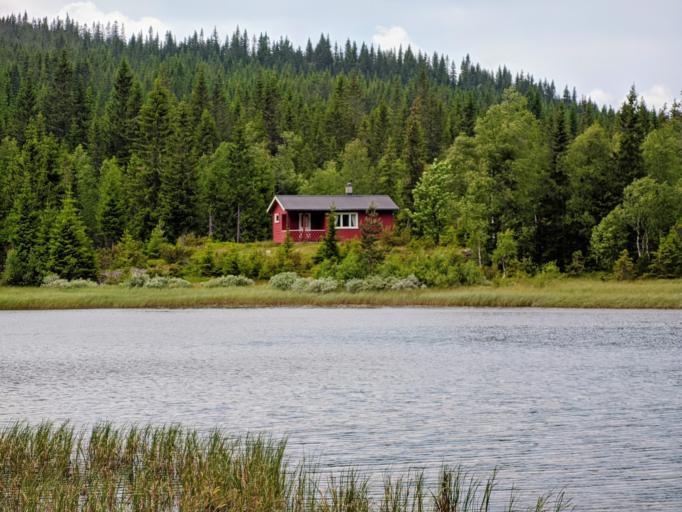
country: NO
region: Akershus
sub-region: Hurdal
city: Hurdal
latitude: 60.5622
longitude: 11.1311
